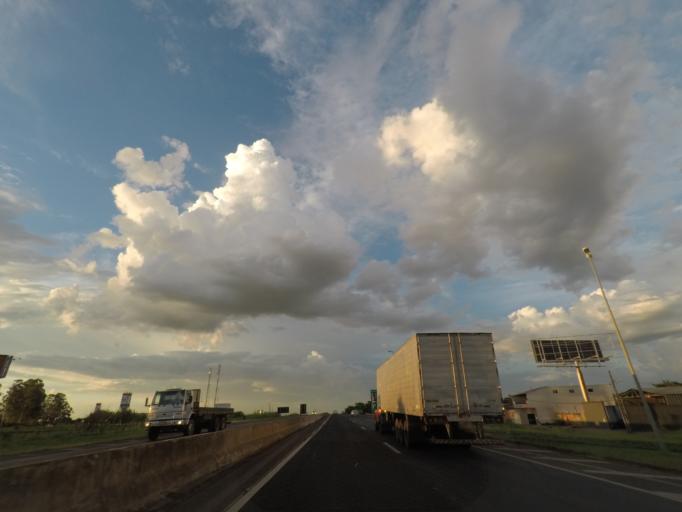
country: BR
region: Minas Gerais
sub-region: Uberaba
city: Uberaba
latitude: -19.7749
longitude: -47.9722
